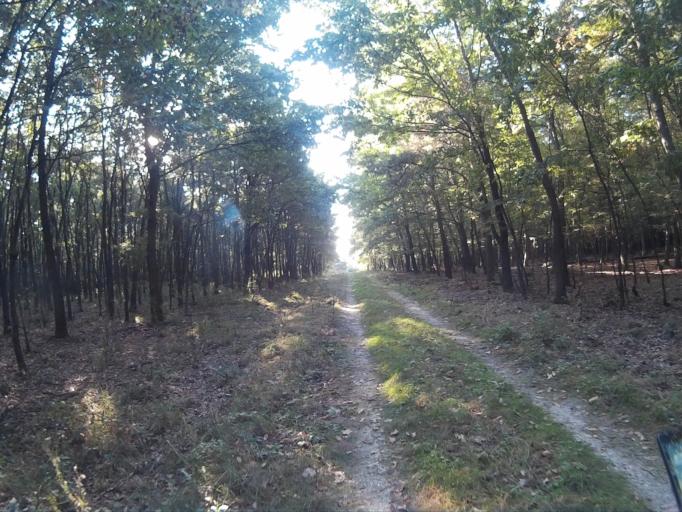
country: HU
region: Vas
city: Jak
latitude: 47.1152
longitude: 16.5960
